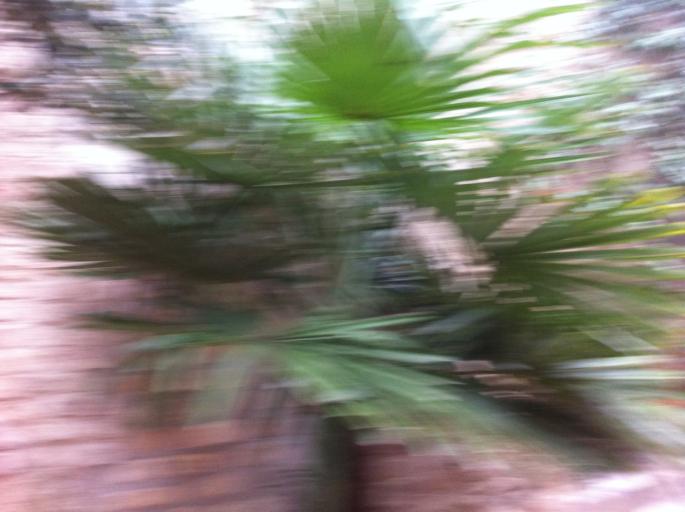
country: IT
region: Umbria
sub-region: Provincia di Perugia
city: Perugia
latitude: 43.1153
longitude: 12.3889
